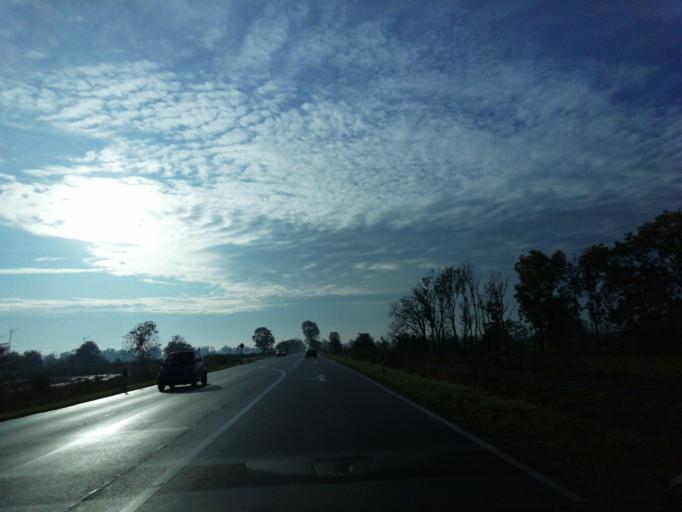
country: DE
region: Lower Saxony
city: Fedderwarden
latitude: 53.6160
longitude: 8.0382
